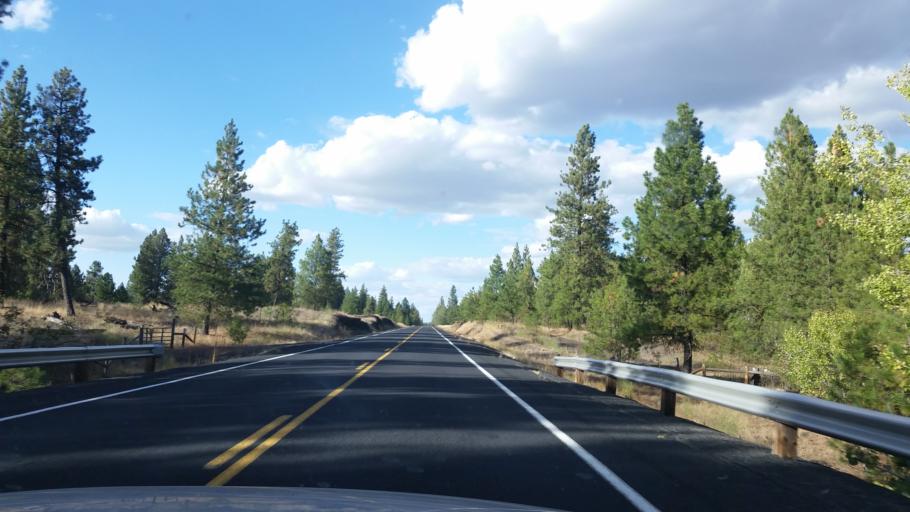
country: US
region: Washington
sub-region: Spokane County
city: Cheney
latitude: 47.4048
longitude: -117.5702
